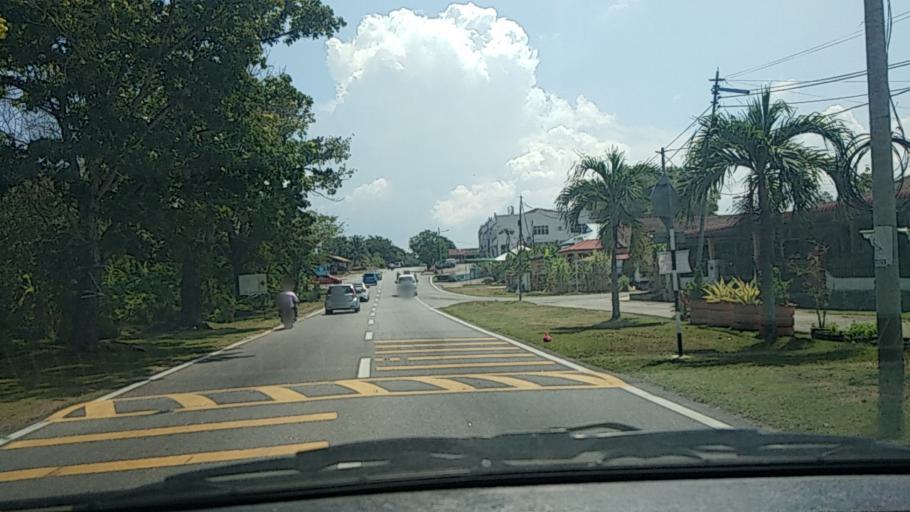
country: MY
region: Kedah
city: Sungai Petani
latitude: 5.6459
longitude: 100.5057
